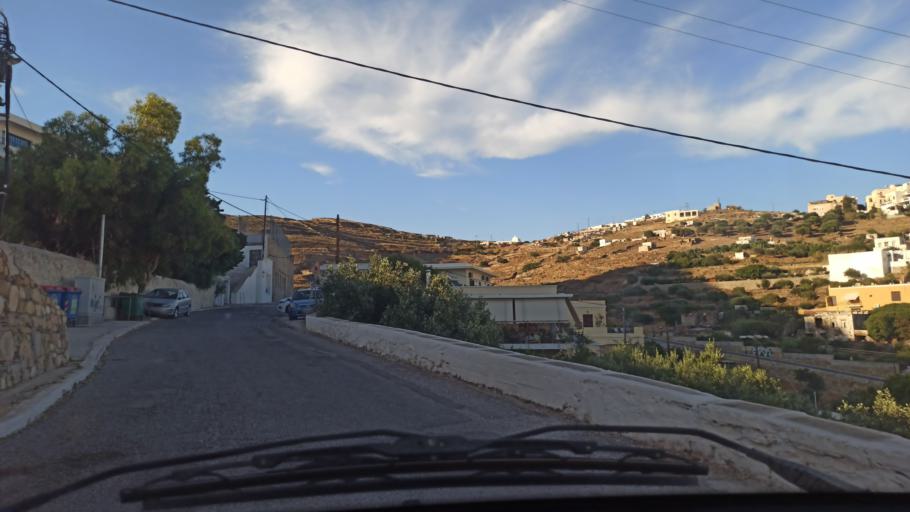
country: GR
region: South Aegean
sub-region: Nomos Kykladon
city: Ano Syros
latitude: 37.4484
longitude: 24.9369
